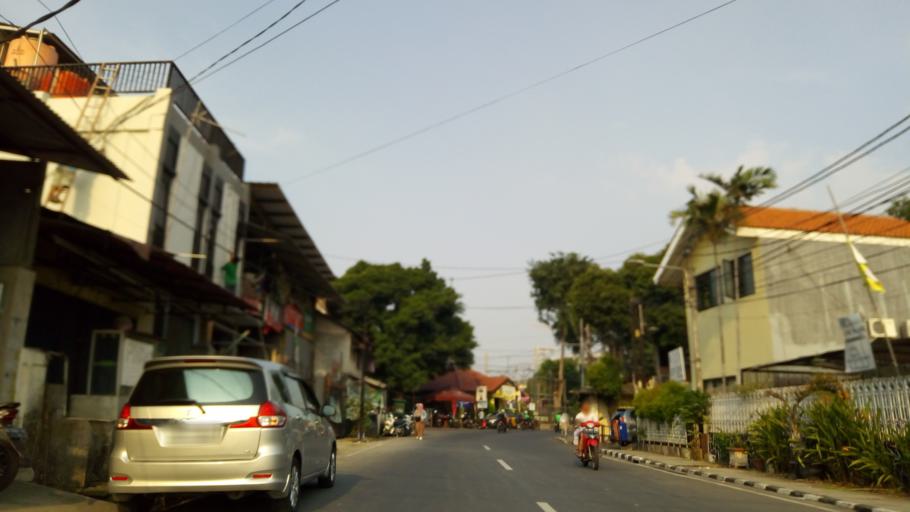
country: ID
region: Jakarta Raya
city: Jakarta
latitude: -6.1933
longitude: 106.8555
